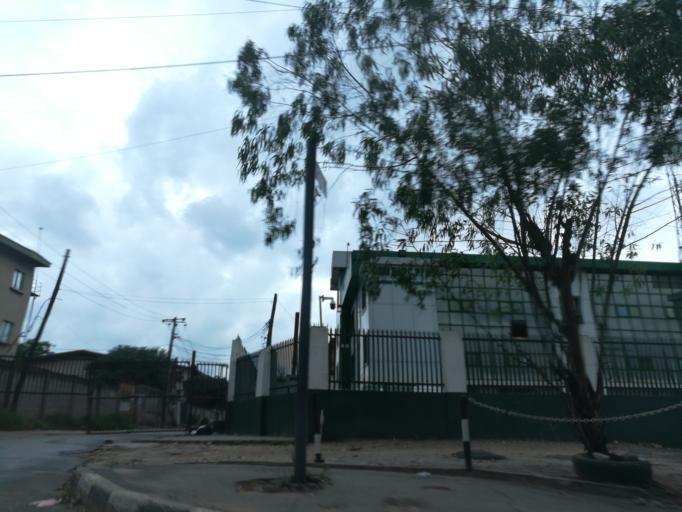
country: NG
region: Lagos
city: Somolu
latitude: 6.5607
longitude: 3.3671
